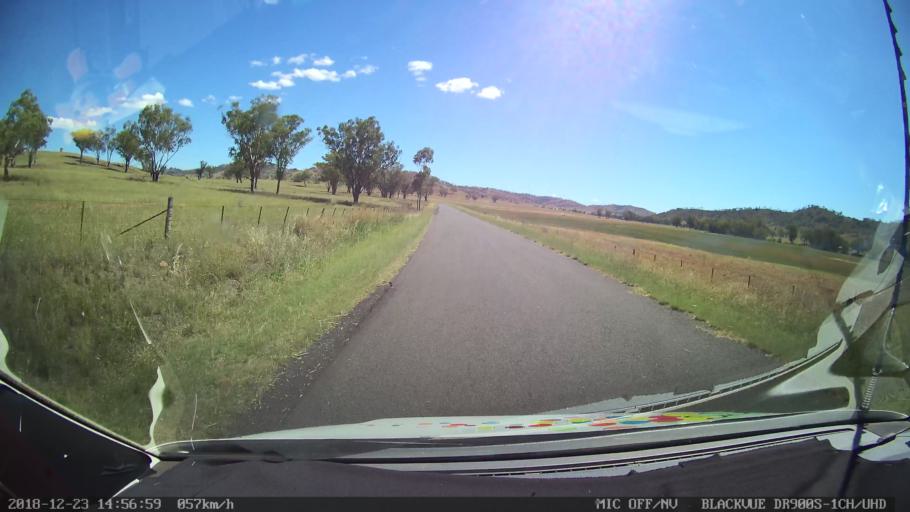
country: AU
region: New South Wales
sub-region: Tamworth Municipality
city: Manilla
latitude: -30.7064
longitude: 150.8286
